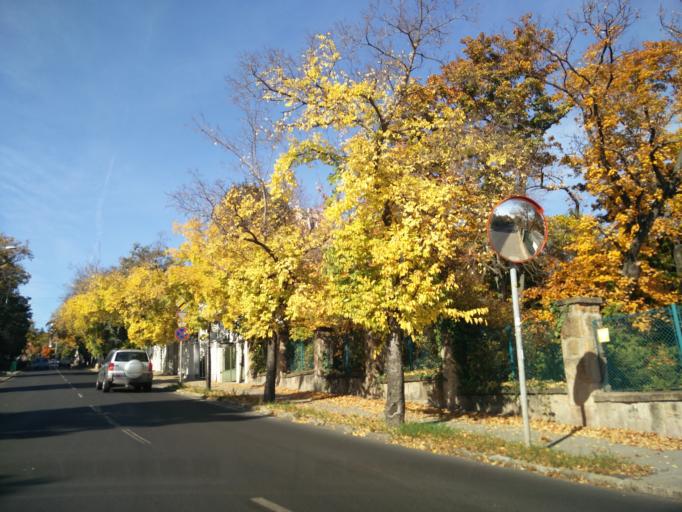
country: HU
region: Budapest
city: Budapest XII. keruelet
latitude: 47.4984
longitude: 19.0101
